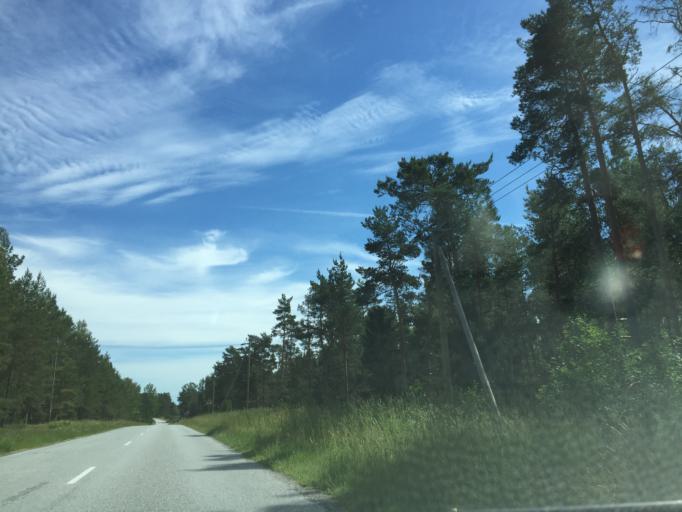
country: LV
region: Rojas
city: Roja
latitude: 57.5796
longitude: 22.6239
